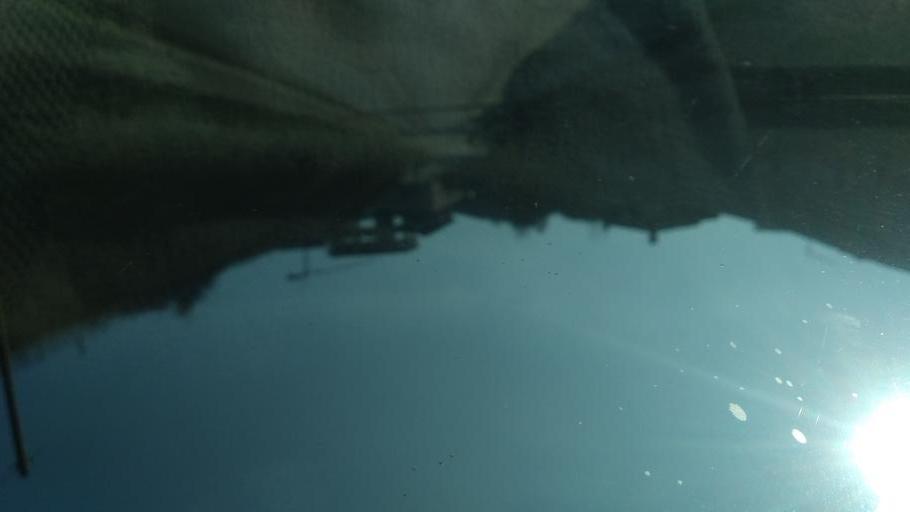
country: XK
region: Pristina
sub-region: Komuna e Prishtines
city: Pristina
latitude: 42.6411
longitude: 21.1561
